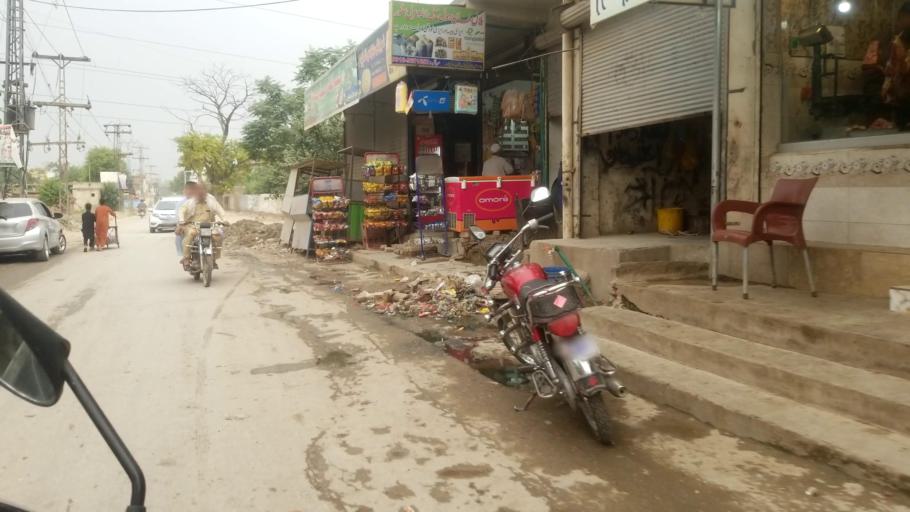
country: PK
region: Khyber Pakhtunkhwa
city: Peshawar
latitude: 33.9843
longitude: 71.5556
